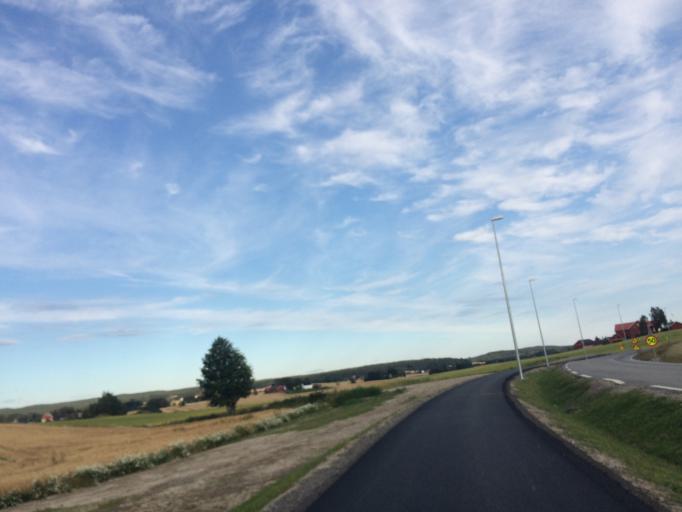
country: NO
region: Akershus
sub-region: Ski
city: Ski
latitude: 59.6960
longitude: 10.8571
